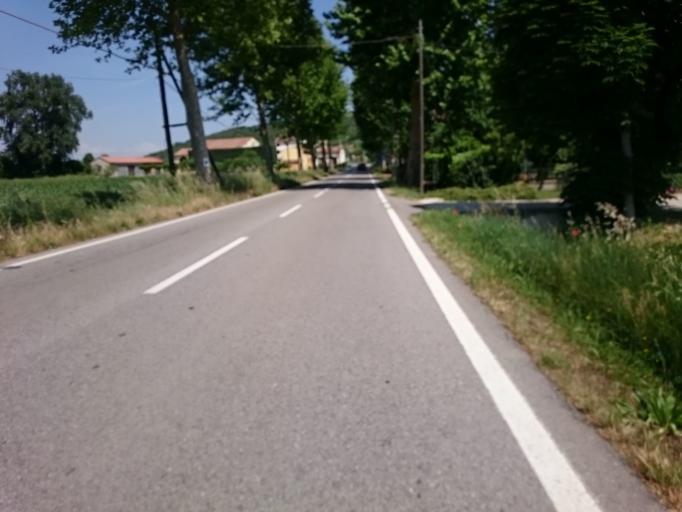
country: IT
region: Veneto
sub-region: Provincia di Padova
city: Lozzo Atestino
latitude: 45.2776
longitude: 11.6162
